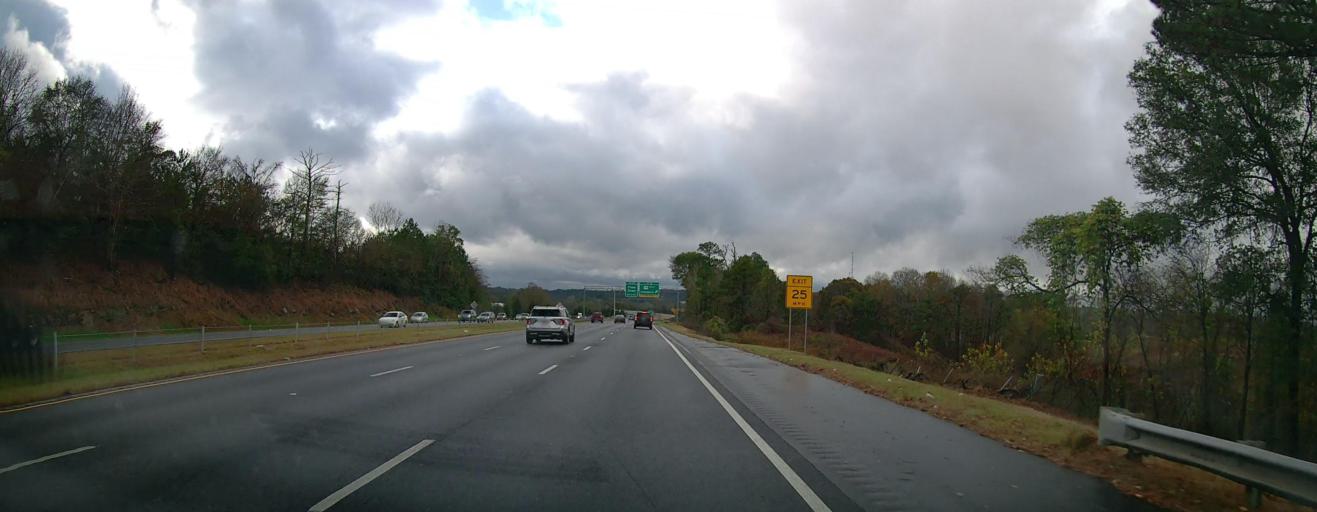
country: US
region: Georgia
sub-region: Clarke County
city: Athens
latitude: 33.9785
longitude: -83.3722
